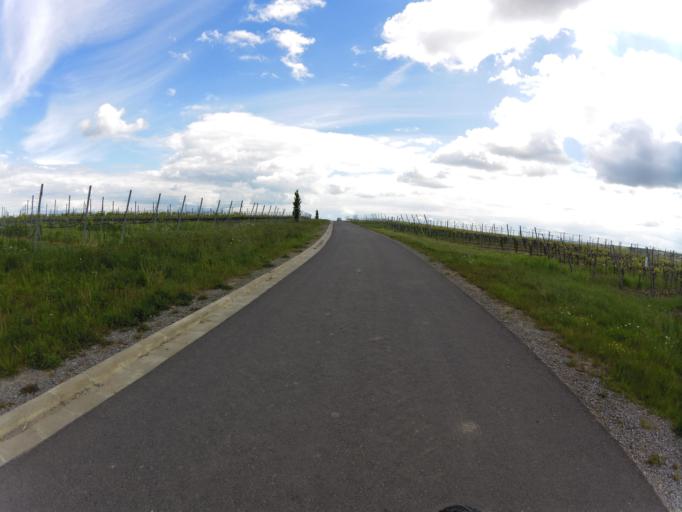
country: DE
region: Bavaria
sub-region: Regierungsbezirk Unterfranken
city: Sommerach
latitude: 49.8426
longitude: 10.1949
